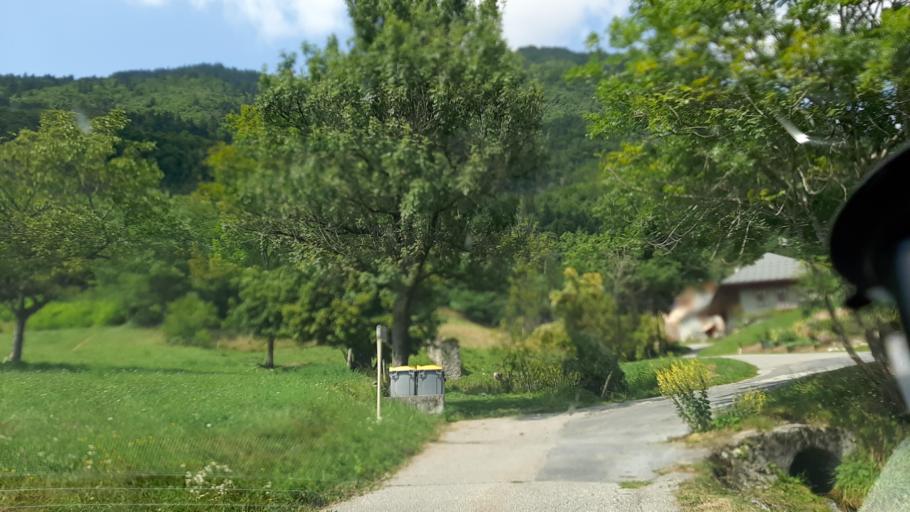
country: FR
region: Rhone-Alpes
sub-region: Departement de la Savoie
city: Mercury
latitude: 45.6779
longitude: 6.3350
